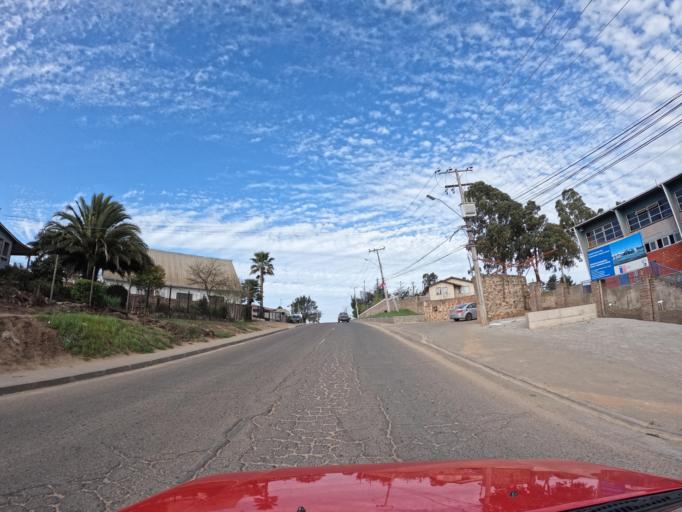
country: CL
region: Valparaiso
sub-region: San Antonio Province
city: San Antonio
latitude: -34.1125
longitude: -71.7240
